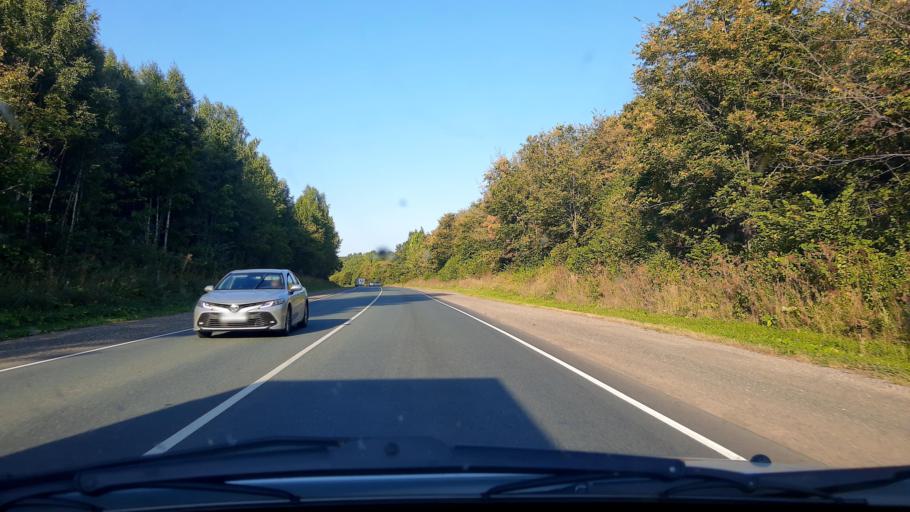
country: RU
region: Bashkortostan
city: Oktyabr'skiy
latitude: 54.4478
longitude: 53.5834
